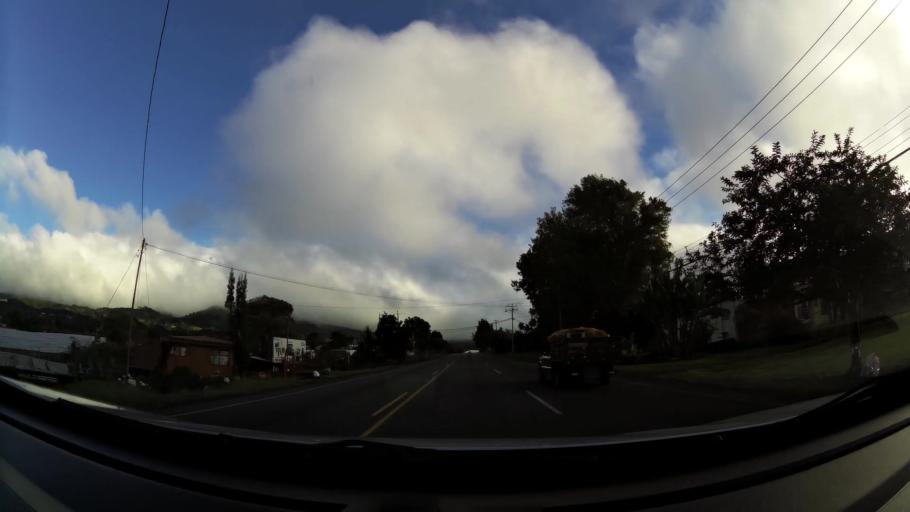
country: CR
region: Heredia
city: Angeles
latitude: 10.0216
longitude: -84.0265
